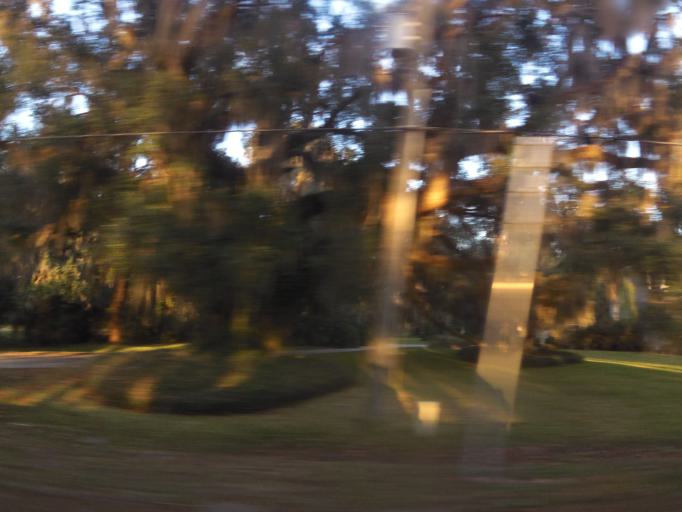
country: US
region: Florida
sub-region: Clay County
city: Green Cove Springs
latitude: 29.9138
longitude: -81.5924
